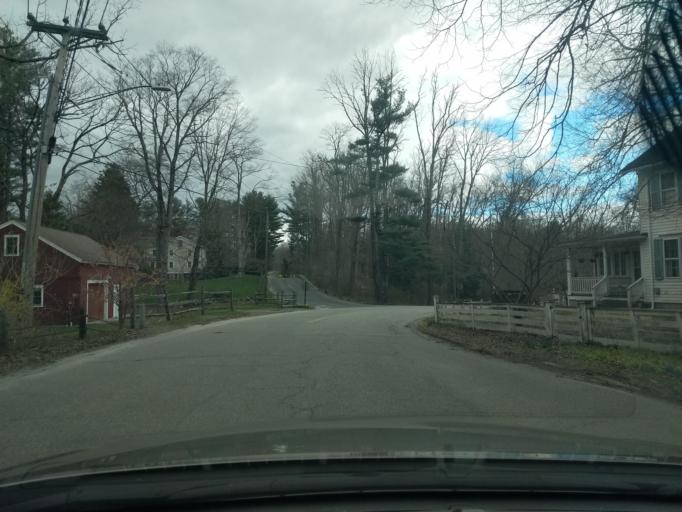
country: US
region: Connecticut
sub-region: Fairfield County
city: Newtown
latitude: 41.3413
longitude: -73.3087
